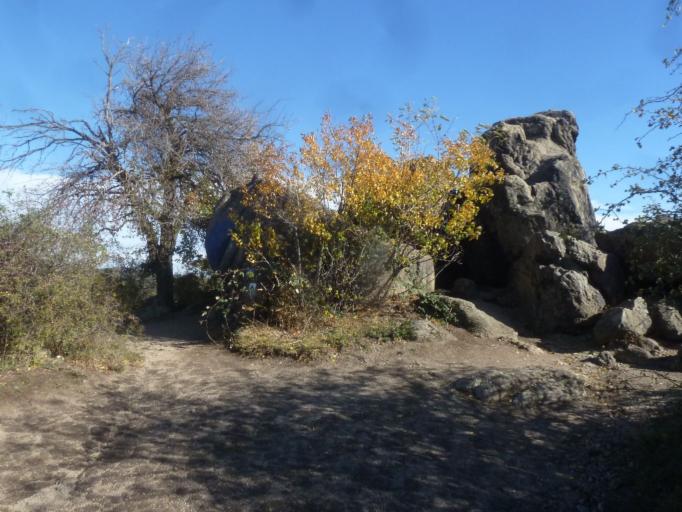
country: HU
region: Fejer
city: Pakozd
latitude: 47.2356
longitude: 18.5380
